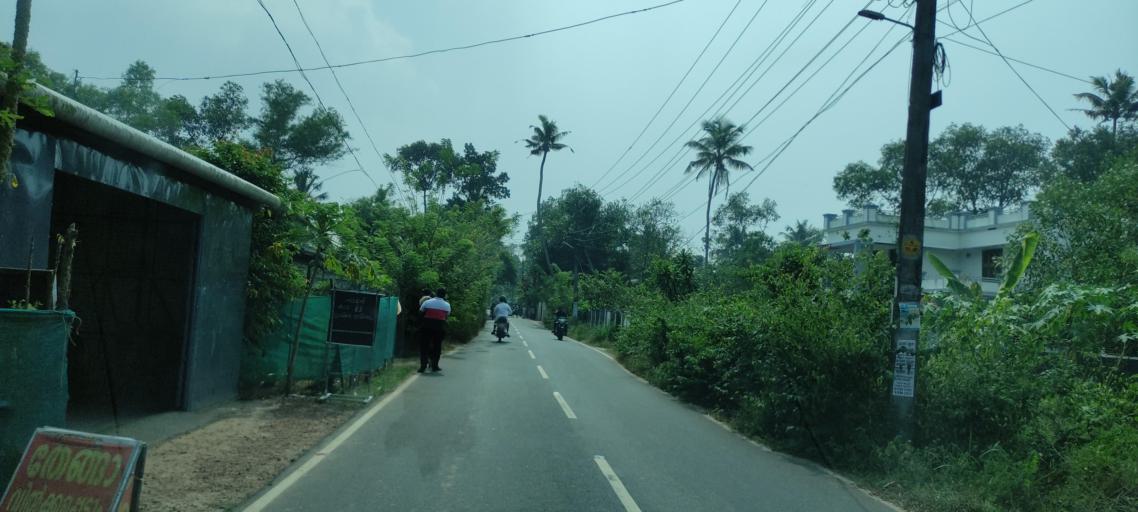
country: IN
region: Kerala
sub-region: Alappuzha
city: Alleppey
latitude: 9.5488
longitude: 76.3329
